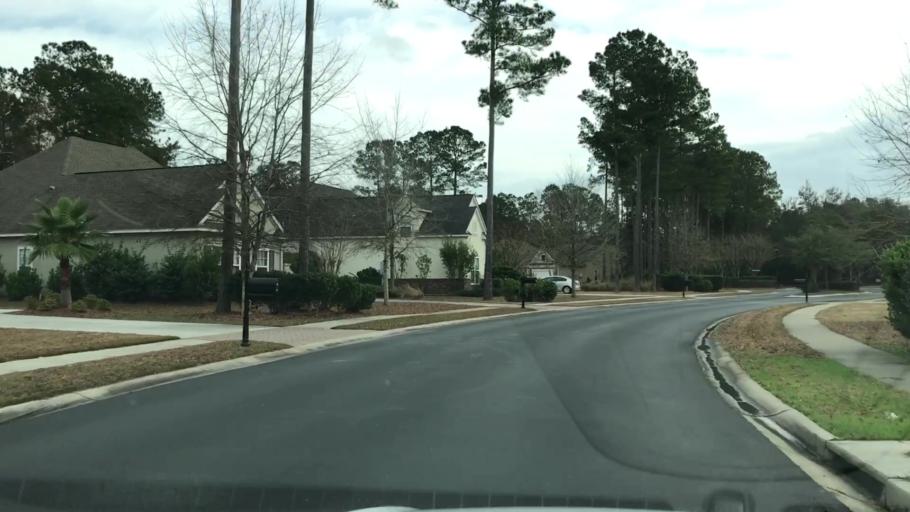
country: US
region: South Carolina
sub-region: Beaufort County
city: Bluffton
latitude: 32.2768
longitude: -80.9316
